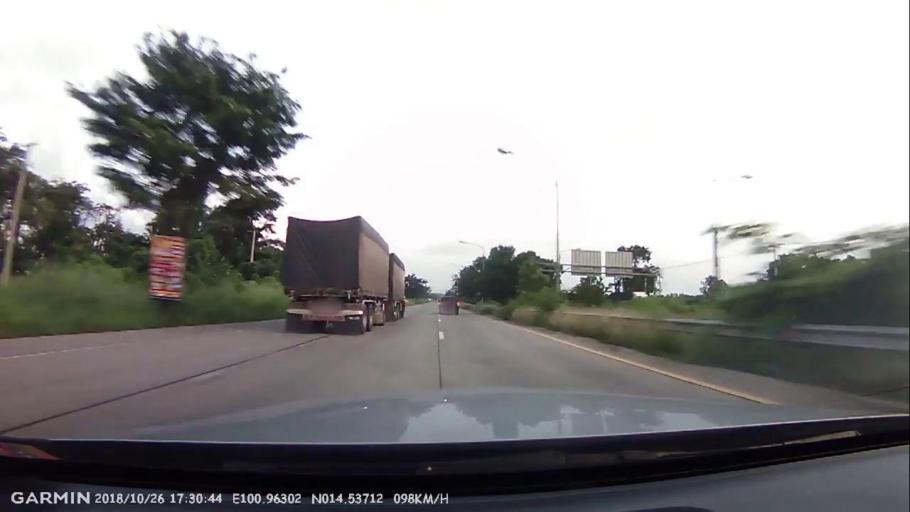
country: TH
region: Sara Buri
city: Saraburi
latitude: 14.5369
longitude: 100.9633
